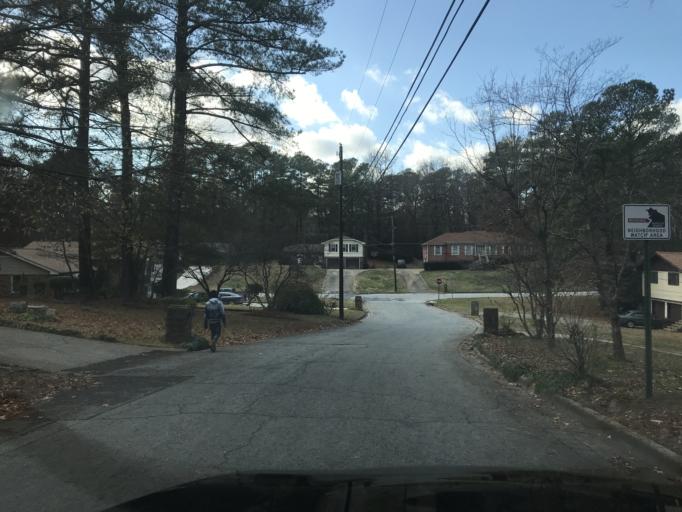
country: US
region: Georgia
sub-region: Fulton County
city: College Park
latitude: 33.6292
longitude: -84.4773
